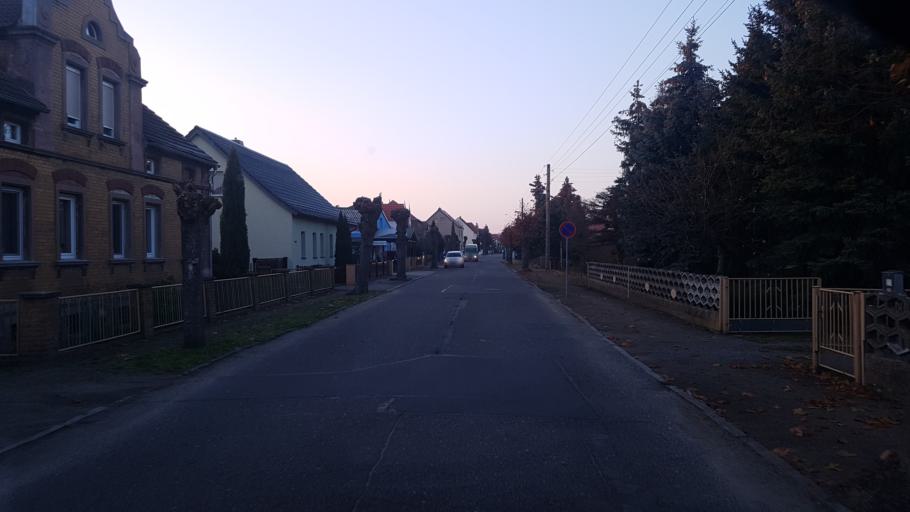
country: DE
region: Brandenburg
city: Lauchhammer
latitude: 51.4720
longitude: 13.7347
